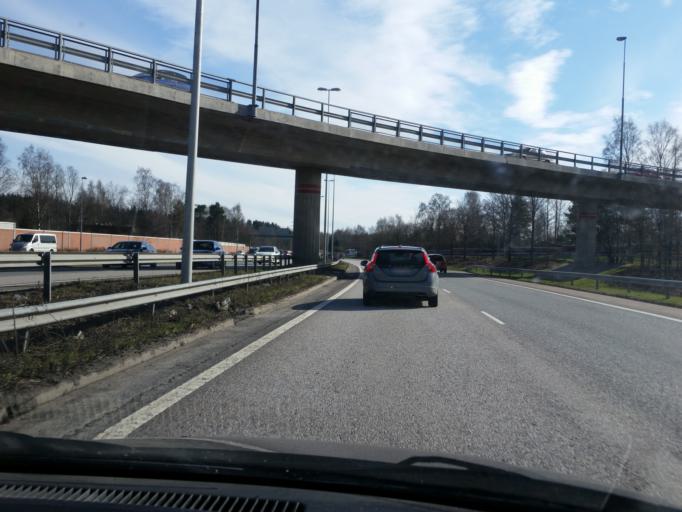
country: FI
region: Uusimaa
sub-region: Helsinki
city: Helsinki
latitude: 60.2434
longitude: 24.9476
